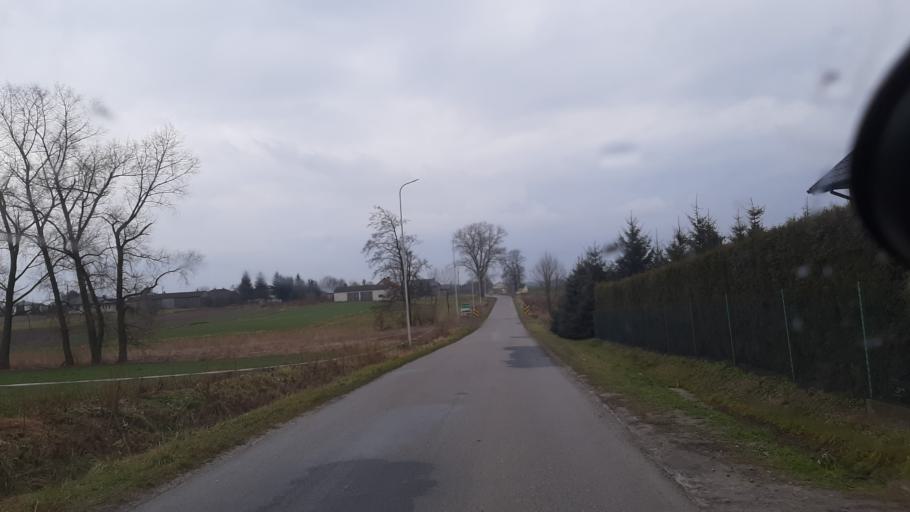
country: PL
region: Lublin Voivodeship
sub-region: Powiat lubelski
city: Jastkow
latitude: 51.3631
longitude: 22.4551
